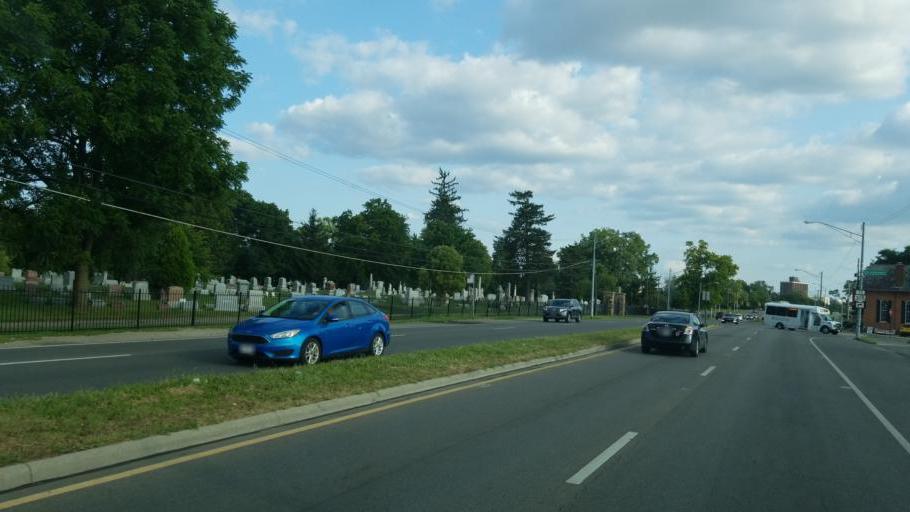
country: US
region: Ohio
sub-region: Franklin County
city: Grandview Heights
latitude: 40.0188
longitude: -83.0241
